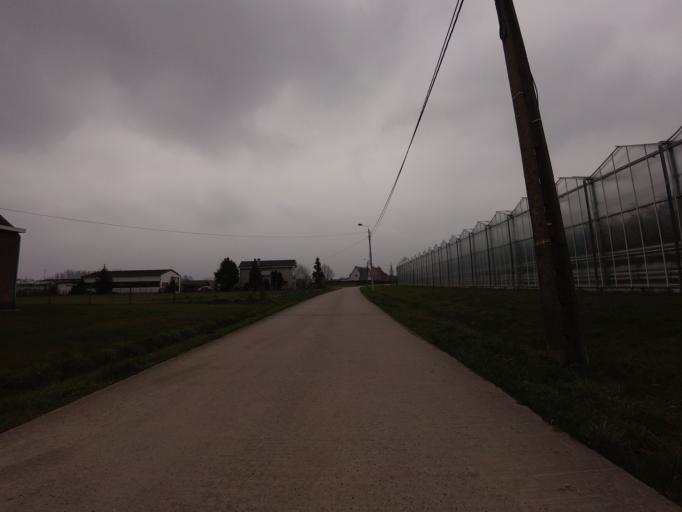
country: BE
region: Flanders
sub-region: Provincie Antwerpen
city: Putte
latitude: 51.0679
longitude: 4.5886
